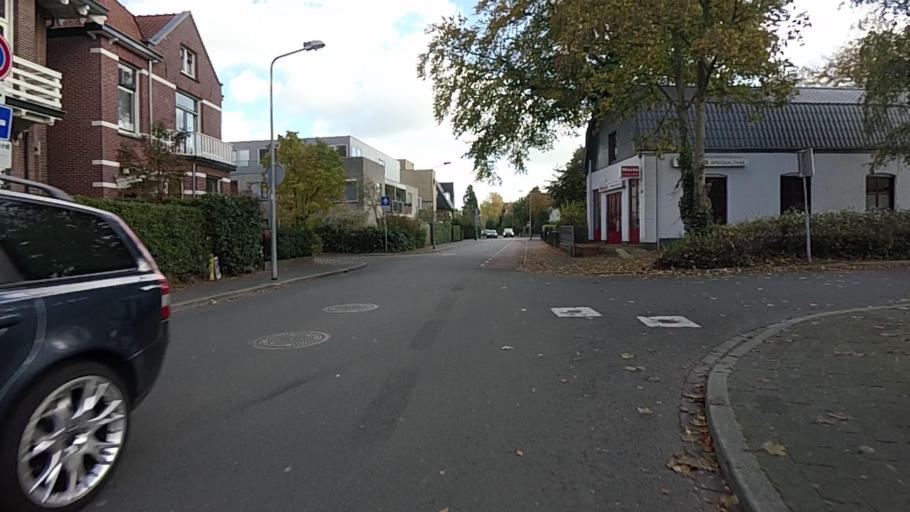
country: NL
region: North Holland
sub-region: Gemeente Hilversum
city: Hilversum
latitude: 52.2205
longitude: 5.1769
